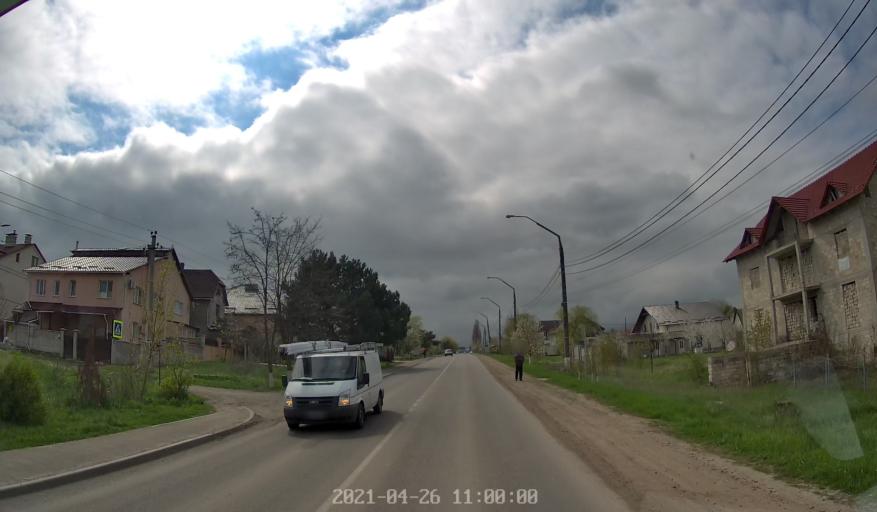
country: MD
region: Chisinau
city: Cricova
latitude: 47.1226
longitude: 28.8662
